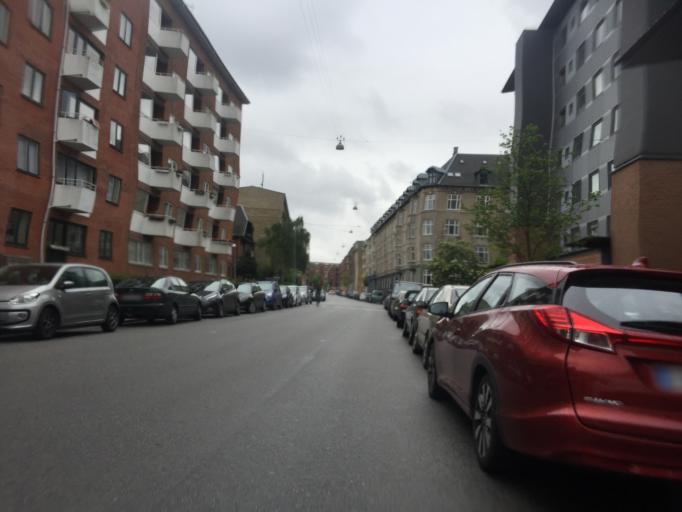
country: DK
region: Capital Region
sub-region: Frederiksberg Kommune
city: Frederiksberg
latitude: 55.6898
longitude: 12.5343
